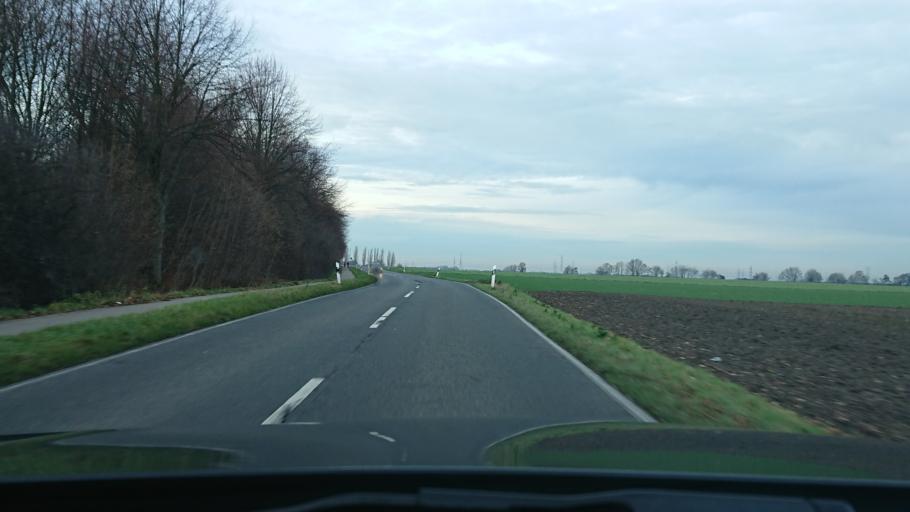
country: DE
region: North Rhine-Westphalia
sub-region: Regierungsbezirk Koln
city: Pulheim
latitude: 50.9782
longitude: 6.7501
